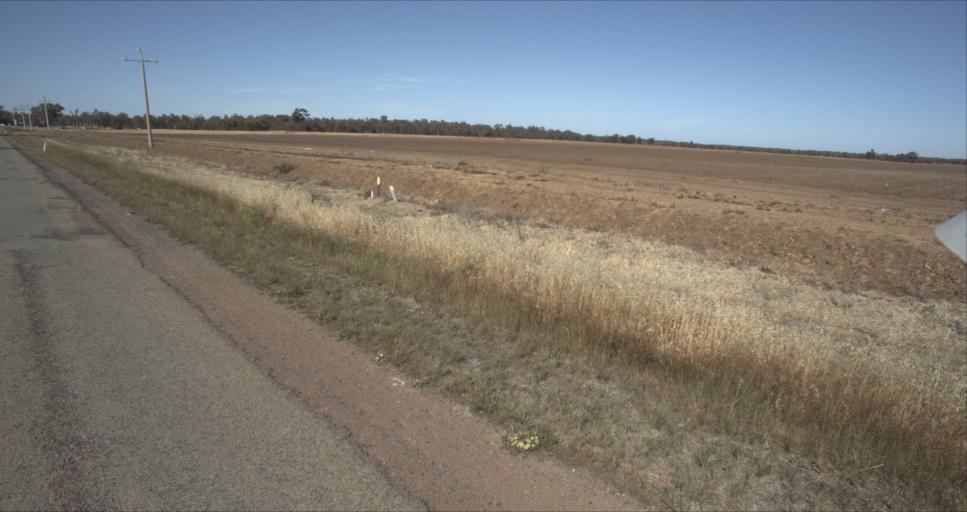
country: AU
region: New South Wales
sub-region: Leeton
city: Leeton
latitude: -34.6019
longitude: 146.2575
